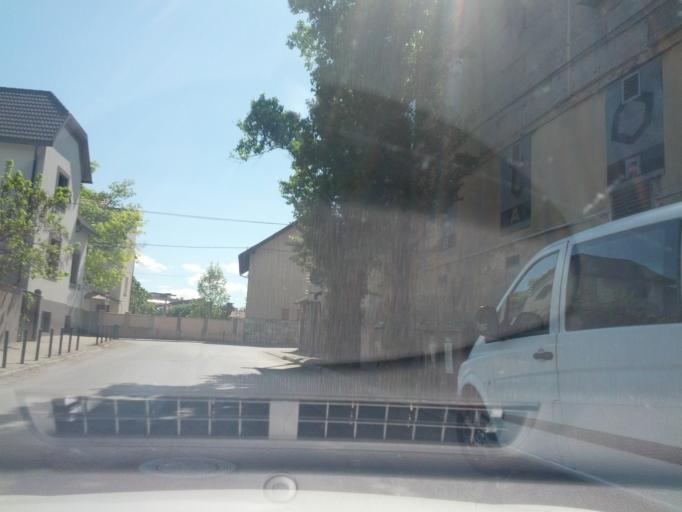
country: SI
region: Ljubljana
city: Ljubljana
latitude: 46.0581
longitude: 14.5217
